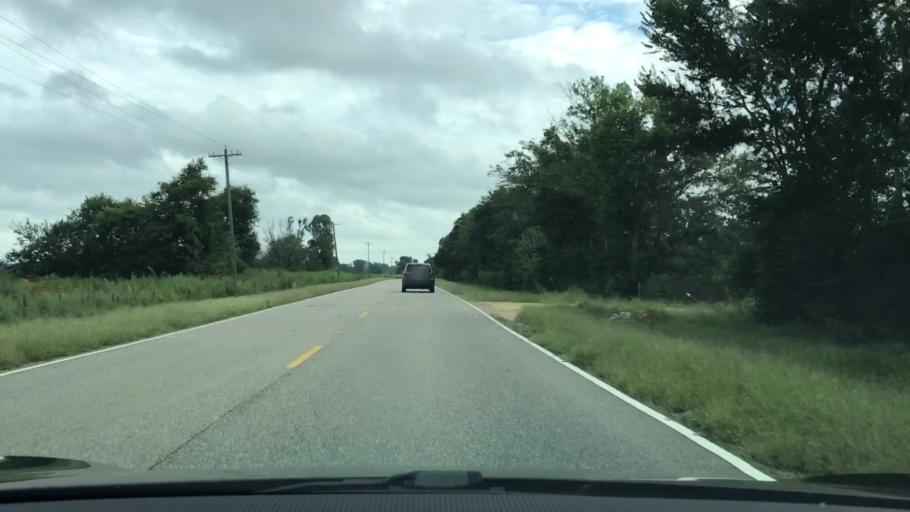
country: US
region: Alabama
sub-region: Montgomery County
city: Pike Road
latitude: 32.2949
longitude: -86.0741
